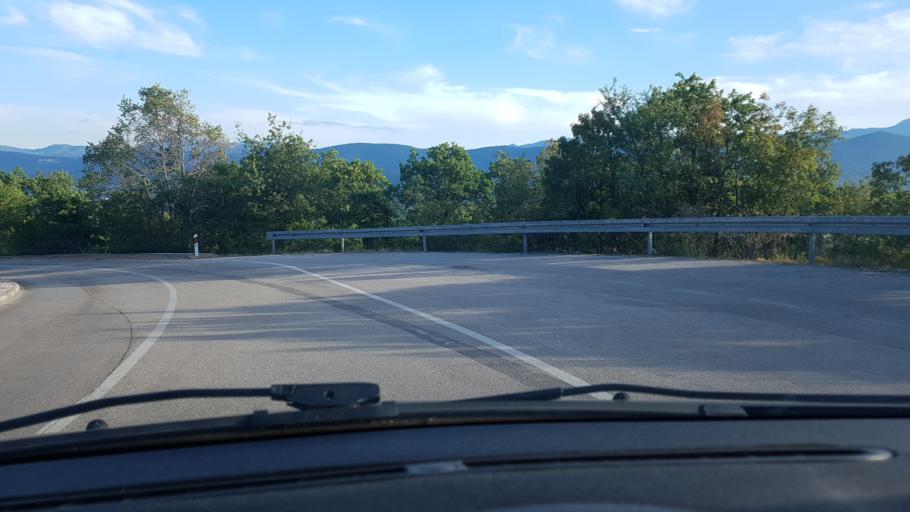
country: HR
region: Splitsko-Dalmatinska
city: Imotski
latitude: 43.4511
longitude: 17.1989
